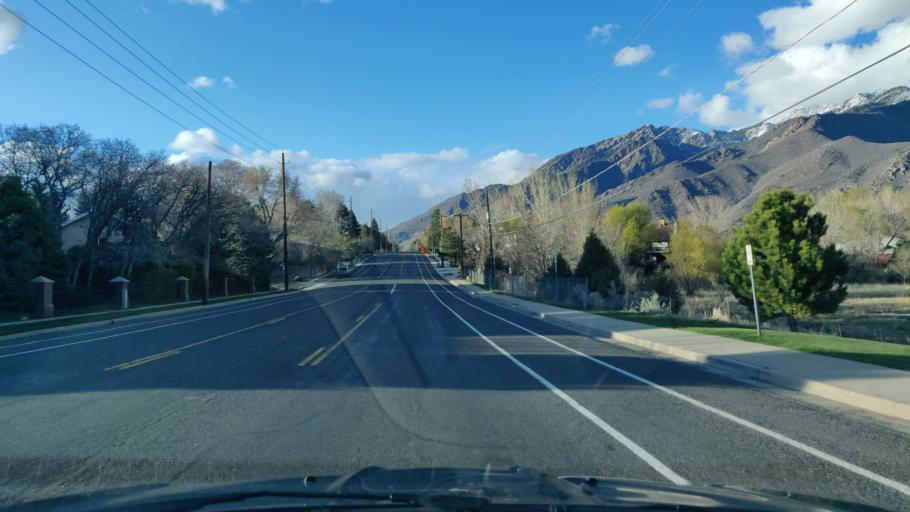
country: US
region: Utah
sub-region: Salt Lake County
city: Cottonwood Heights
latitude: 40.6040
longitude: -111.7959
